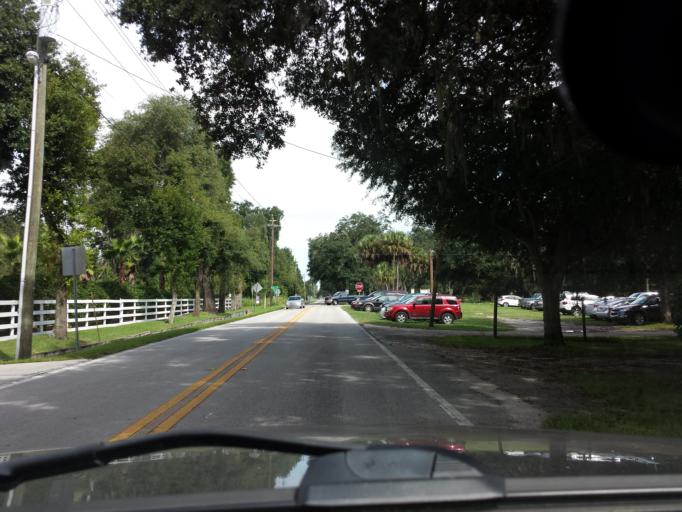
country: US
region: Florida
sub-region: Hillsborough County
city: Dover
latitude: 28.0470
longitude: -82.1880
